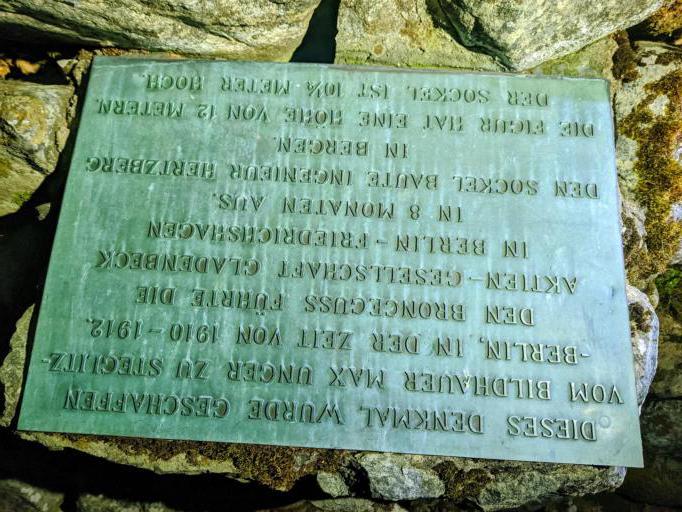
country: NO
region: Sogn og Fjordane
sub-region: Vik
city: Vikoyri
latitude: 61.1722
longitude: 6.6402
